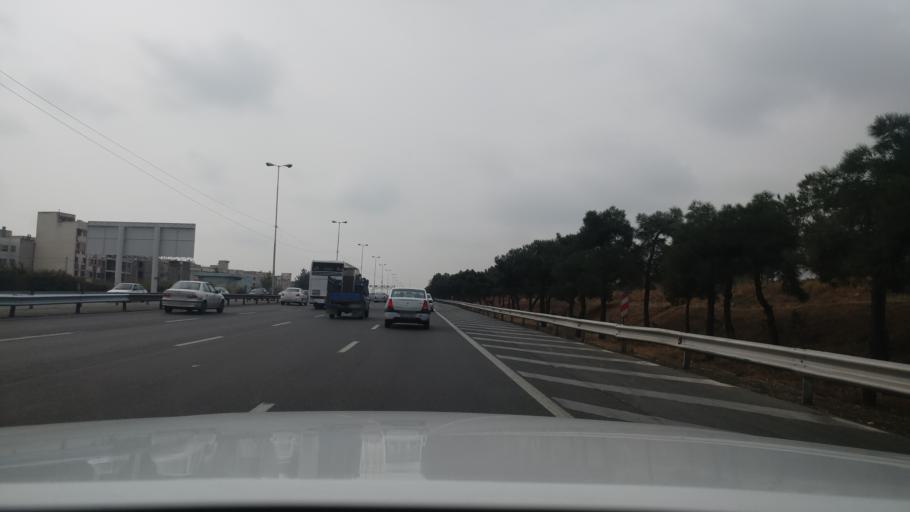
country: IR
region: Tehran
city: Tehran
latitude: 35.7159
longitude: 51.2805
